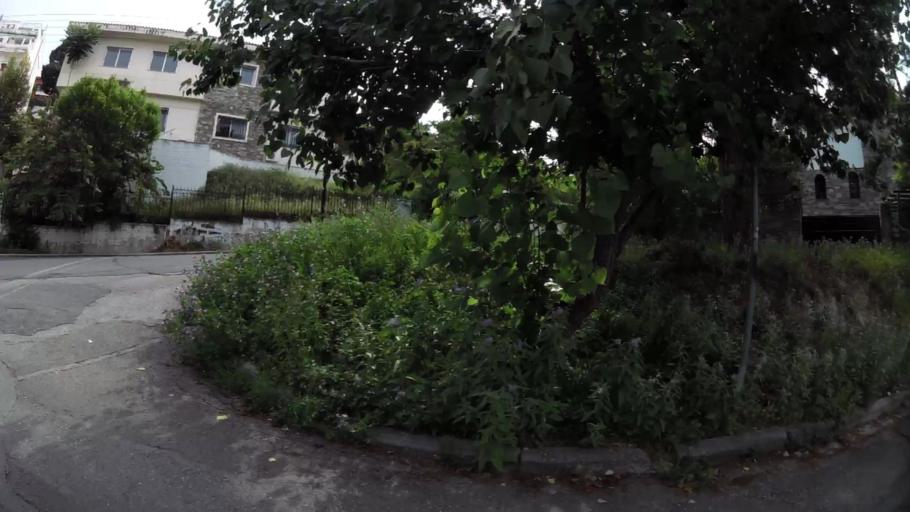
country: GR
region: Central Macedonia
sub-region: Nomos Thessalonikis
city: Panorama
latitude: 40.5845
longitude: 23.0309
